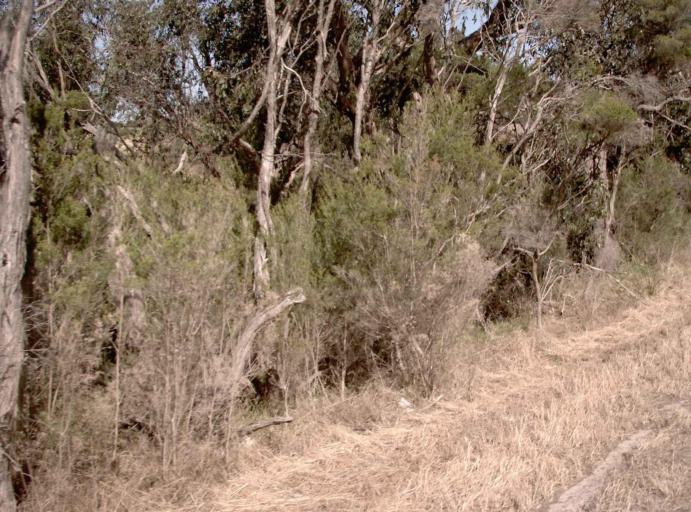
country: AU
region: Victoria
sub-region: Wellington
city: Sale
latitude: -38.3231
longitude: 147.1593
